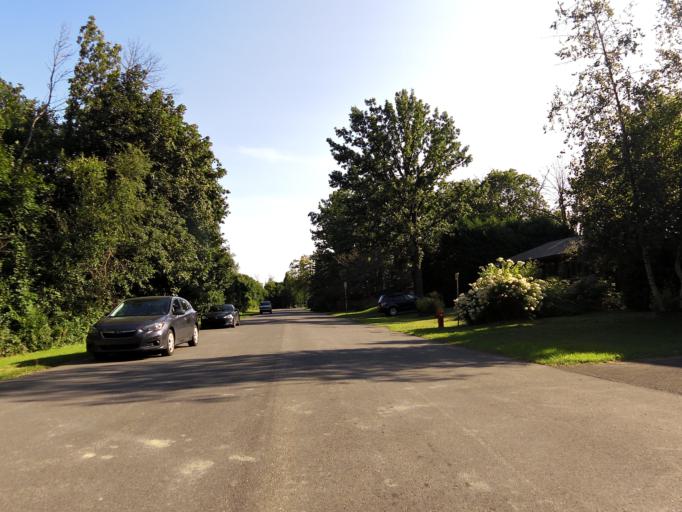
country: CA
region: Ontario
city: Ottawa
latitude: 45.4245
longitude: -75.7471
